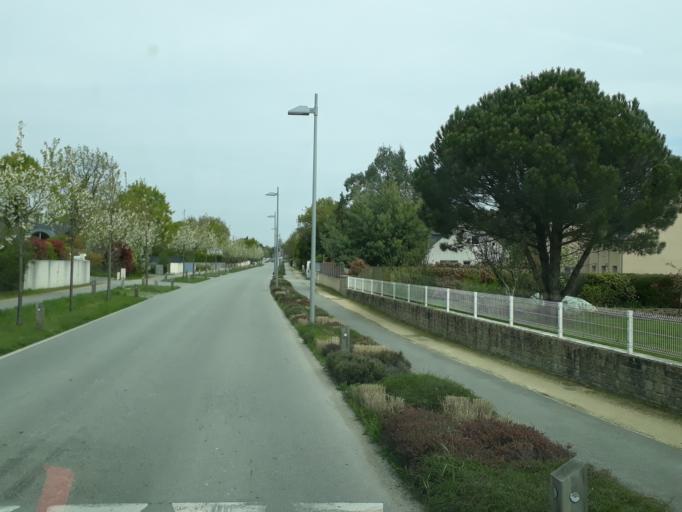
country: FR
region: Brittany
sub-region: Departement du Morbihan
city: Surzur
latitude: 47.5840
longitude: -2.6290
